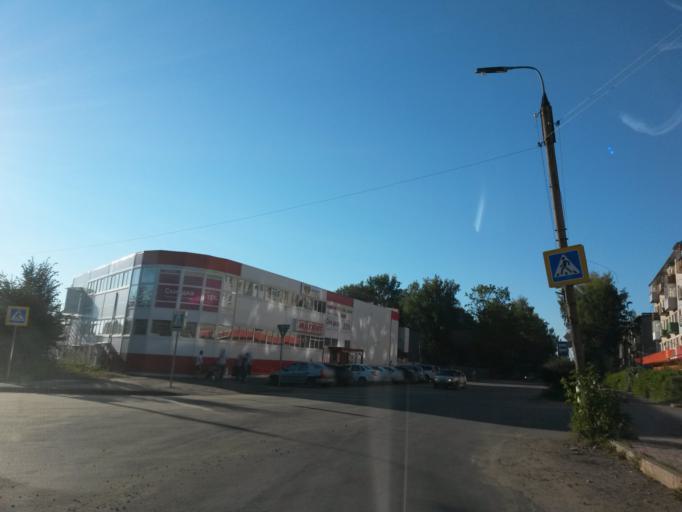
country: RU
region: Jaroslavl
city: Gavrilov-Yam
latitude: 57.2997
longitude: 39.8646
